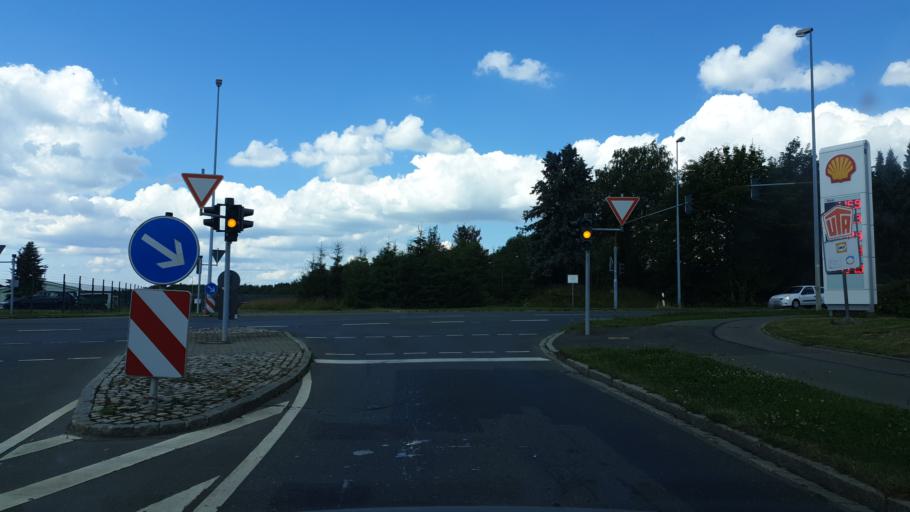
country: DE
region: Saxony
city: Marienberg
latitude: 50.6581
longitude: 13.1536
